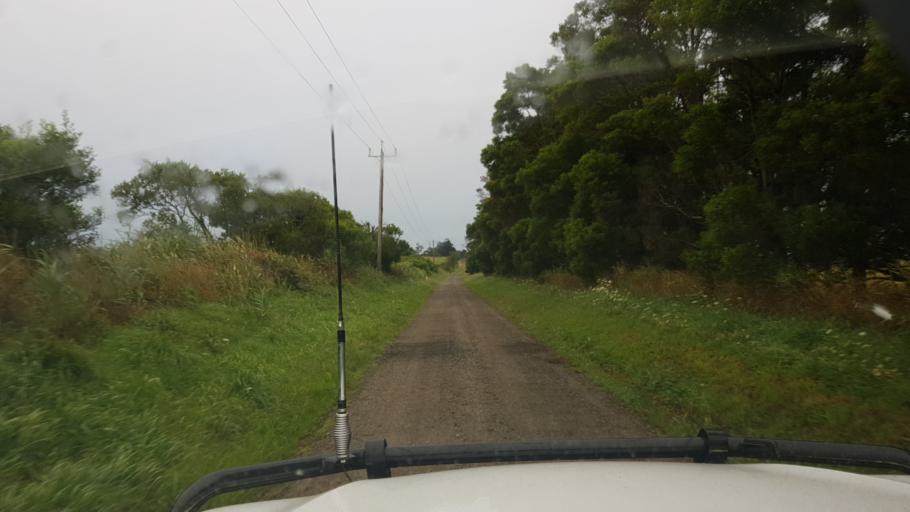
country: AU
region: Victoria
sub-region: Latrobe
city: Moe
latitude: -38.1685
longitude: 146.1944
